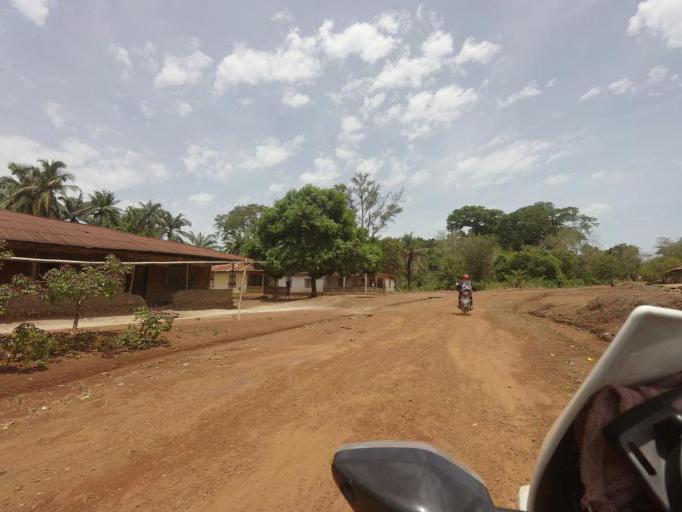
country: SL
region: Northern Province
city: Kamakwie
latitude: 9.5093
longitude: -12.2664
